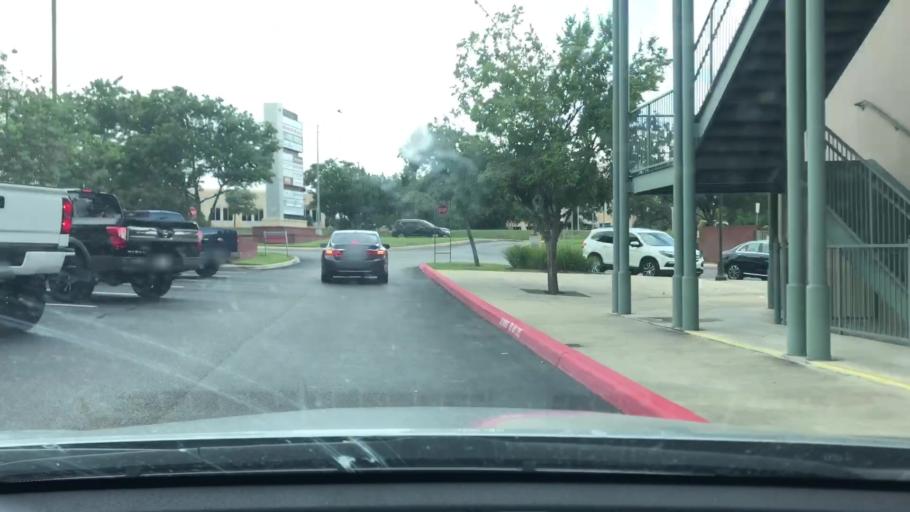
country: US
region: Texas
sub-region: Bexar County
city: Hollywood Park
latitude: 29.6143
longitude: -98.4845
